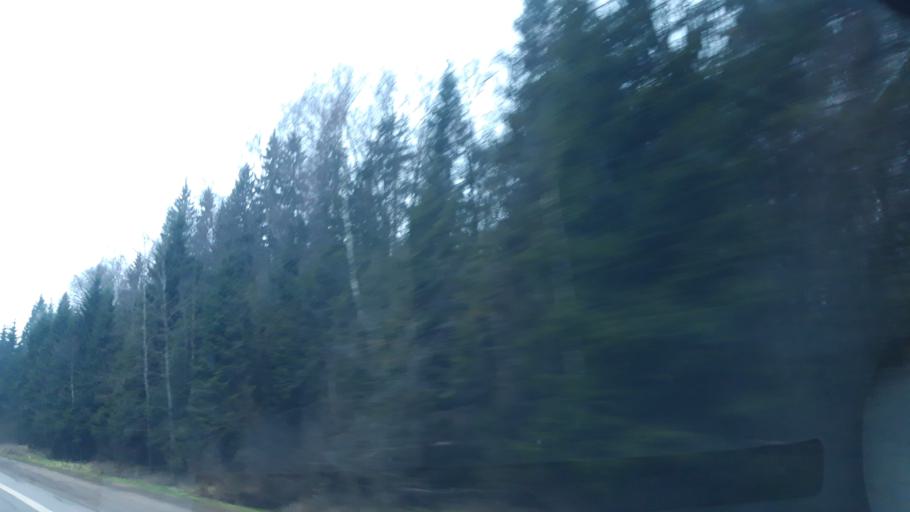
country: RU
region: Moskovskaya
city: Istra
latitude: 56.0529
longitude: 36.8964
